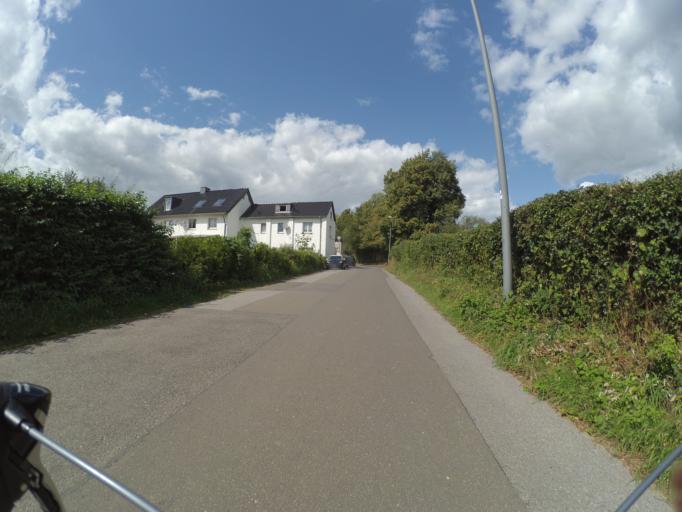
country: DE
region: North Rhine-Westphalia
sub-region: Regierungsbezirk Koln
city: Aachen
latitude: 50.8025
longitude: 6.0930
